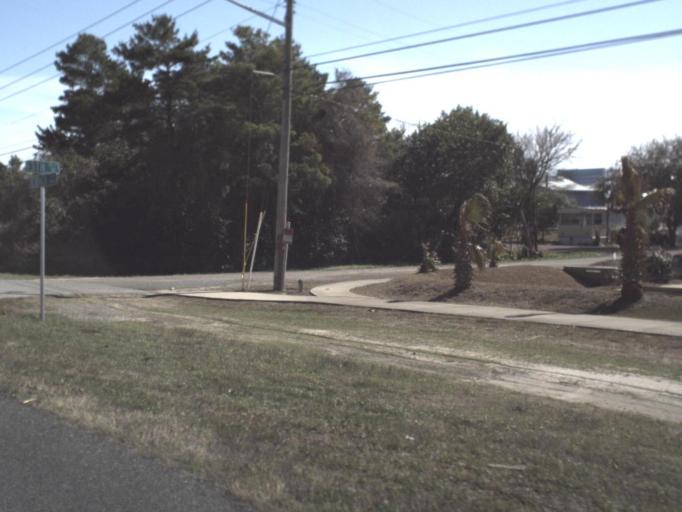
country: US
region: Florida
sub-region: Bay County
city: Laguna Beach
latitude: 30.2491
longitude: -85.9305
